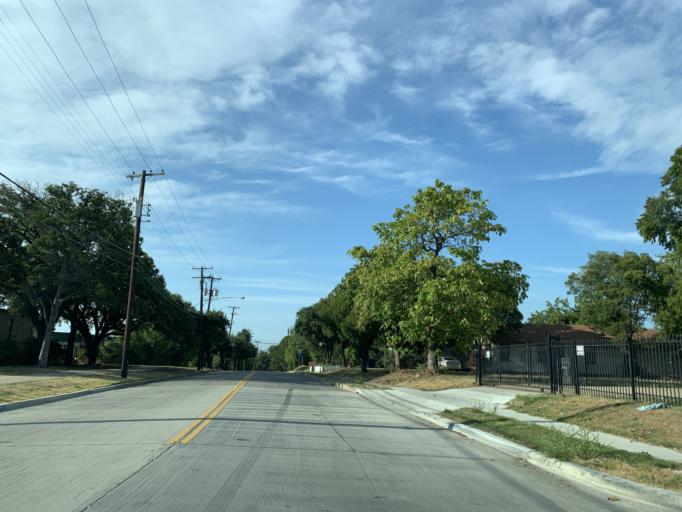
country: US
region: Texas
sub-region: Dallas County
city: Dallas
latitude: 32.7364
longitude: -96.8114
